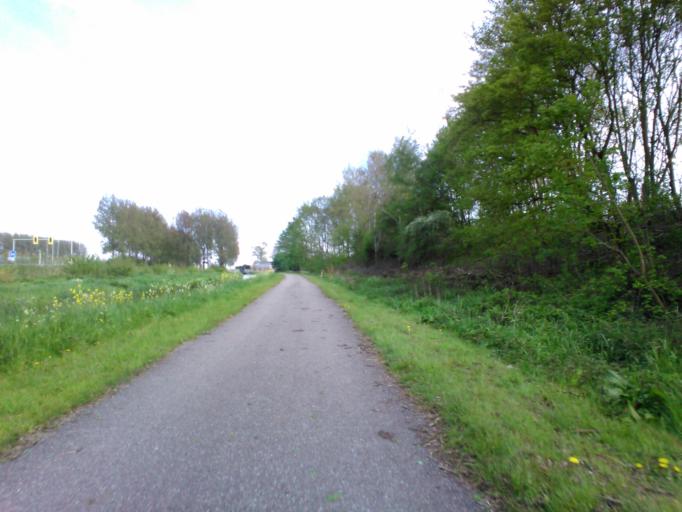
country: NL
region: South Holland
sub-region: Bodegraven-Reeuwijk
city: Bodegraven
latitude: 52.0656
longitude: 4.7503
